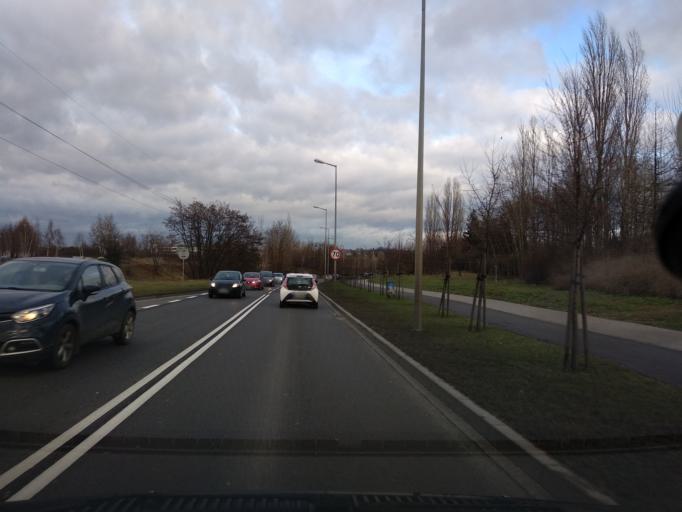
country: PL
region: Greater Poland Voivodeship
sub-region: Kalisz
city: Kalisz
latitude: 51.7658
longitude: 18.0639
